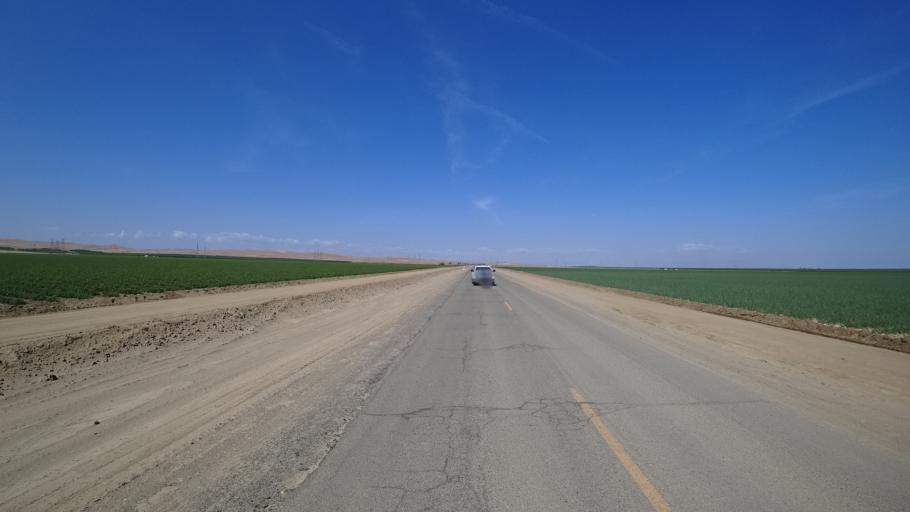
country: US
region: California
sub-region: Kings County
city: Avenal
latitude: 36.0725
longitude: -120.0493
